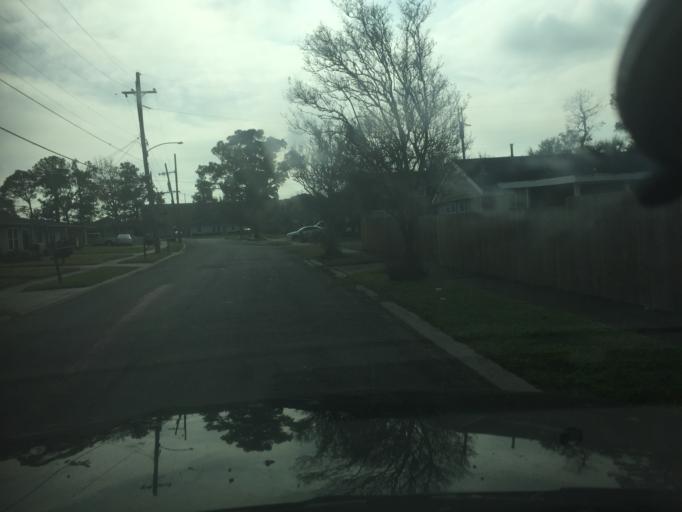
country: US
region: Louisiana
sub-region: Saint Bernard Parish
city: Arabi
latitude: 30.0078
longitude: -90.0384
